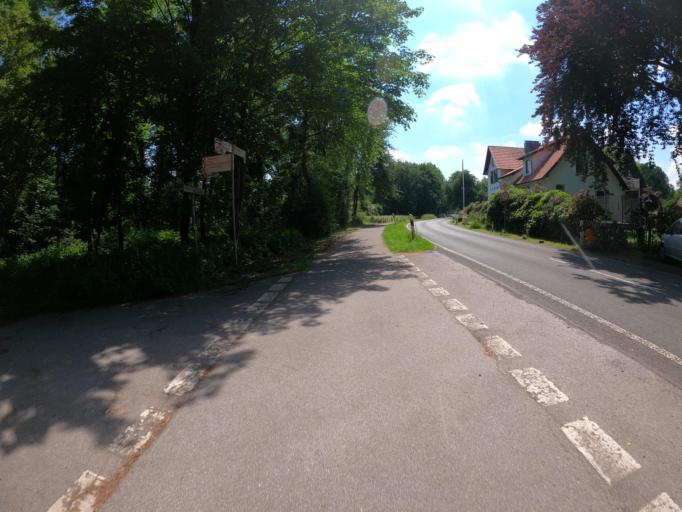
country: DE
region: North Rhine-Westphalia
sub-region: Regierungsbezirk Dusseldorf
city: Hunxe
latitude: 51.7103
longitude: 6.7791
